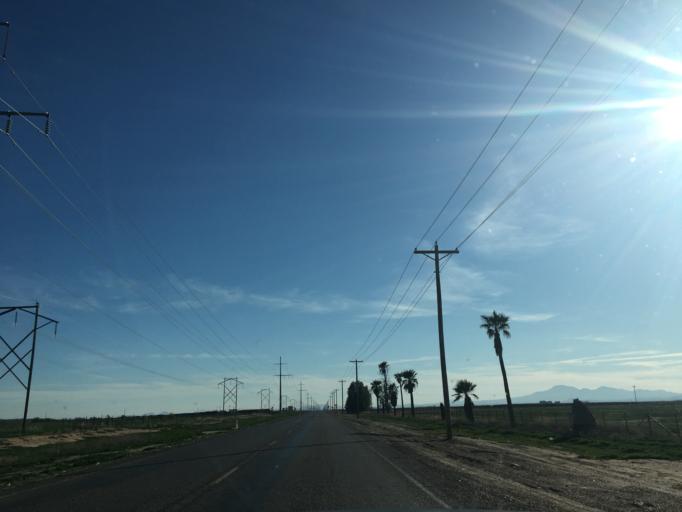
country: US
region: Arizona
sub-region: Pinal County
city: Maricopa
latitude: 33.0208
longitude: -111.9965
